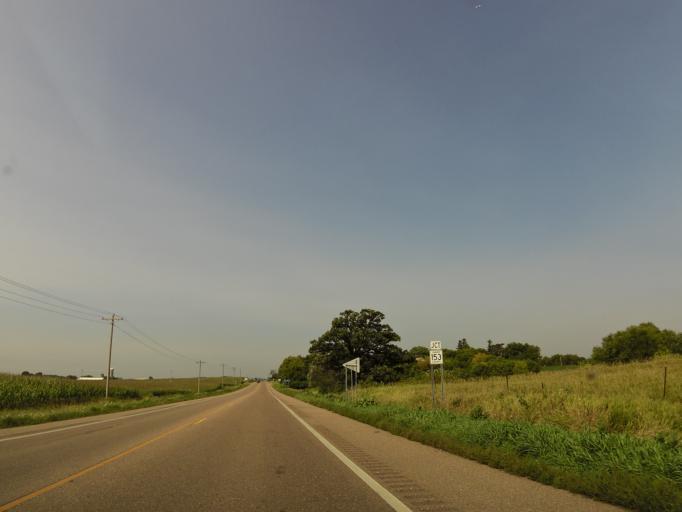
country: US
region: Minnesota
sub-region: Carver County
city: Cologne
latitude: 44.7671
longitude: -93.8237
